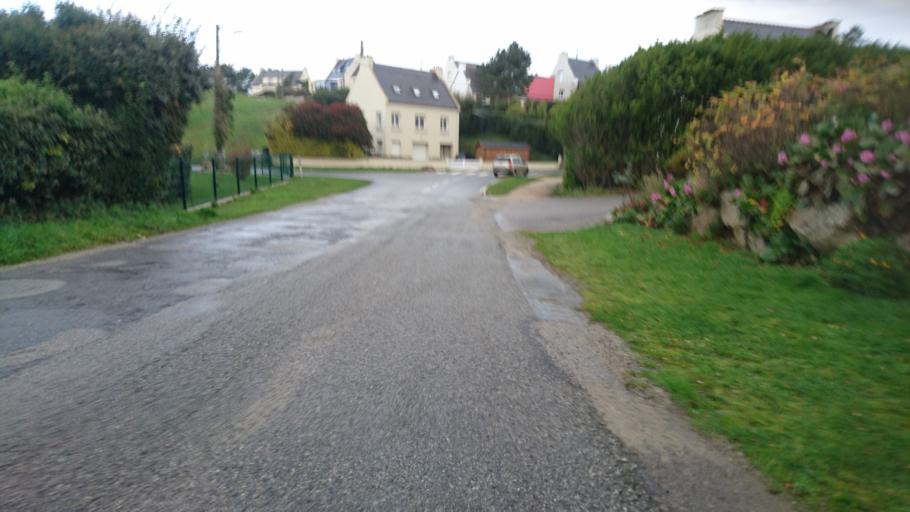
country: FR
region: Brittany
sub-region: Departement du Finistere
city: Lampaul-Plouarzel
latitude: 48.4439
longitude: -4.7700
